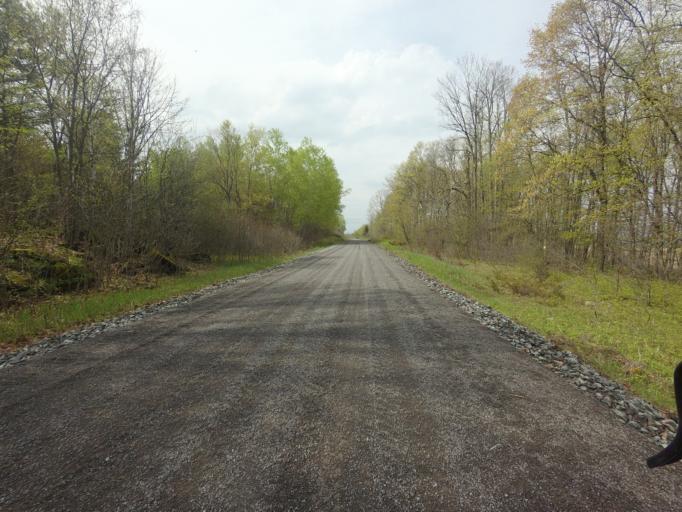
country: CA
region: Ontario
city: Carleton Place
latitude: 45.1612
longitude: -76.1462
